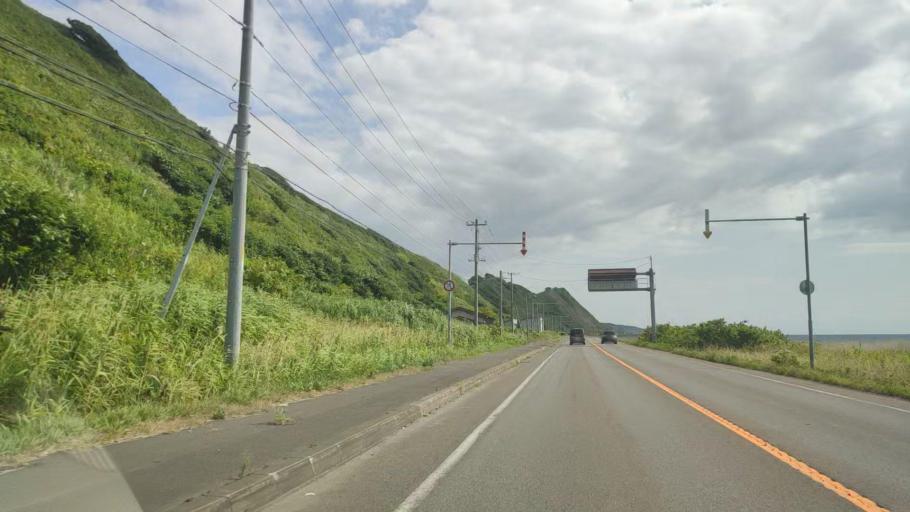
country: JP
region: Hokkaido
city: Rumoi
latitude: 44.2196
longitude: 141.6555
